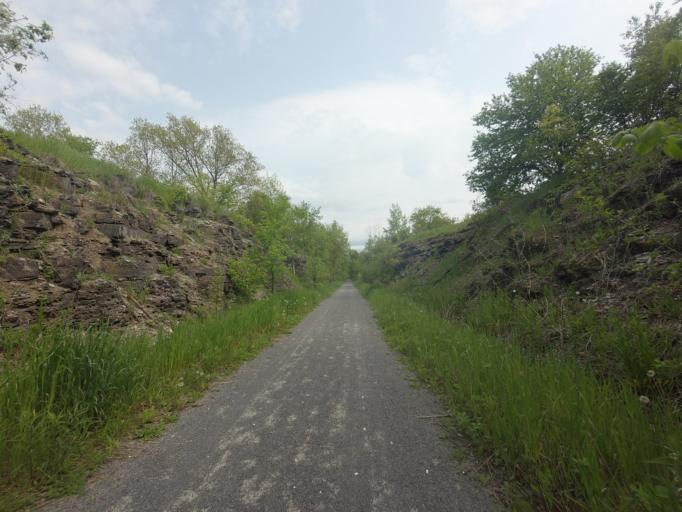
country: CA
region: Ontario
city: Kingston
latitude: 44.4126
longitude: -76.6211
